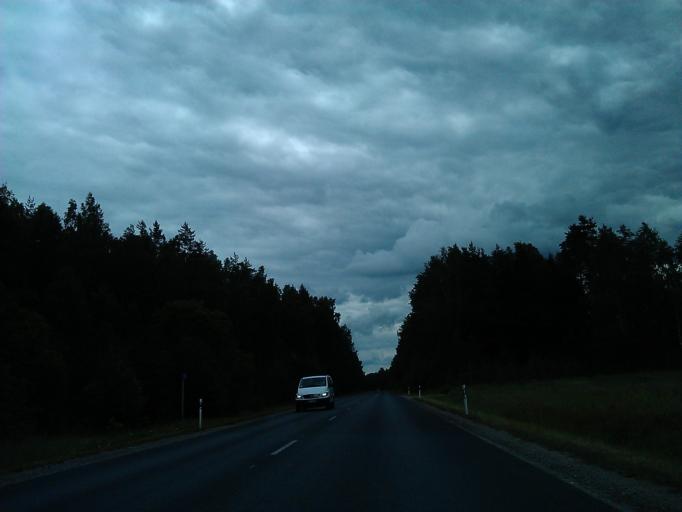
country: LV
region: Dobeles Rajons
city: Dobele
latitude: 56.6529
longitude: 23.2005
